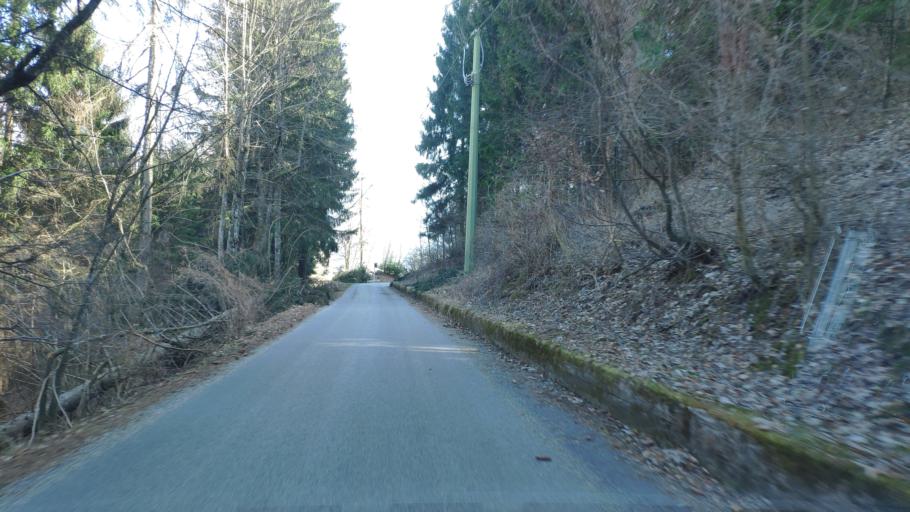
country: IT
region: Veneto
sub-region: Provincia di Vicenza
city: Enego
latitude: 45.9571
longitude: 11.6892
